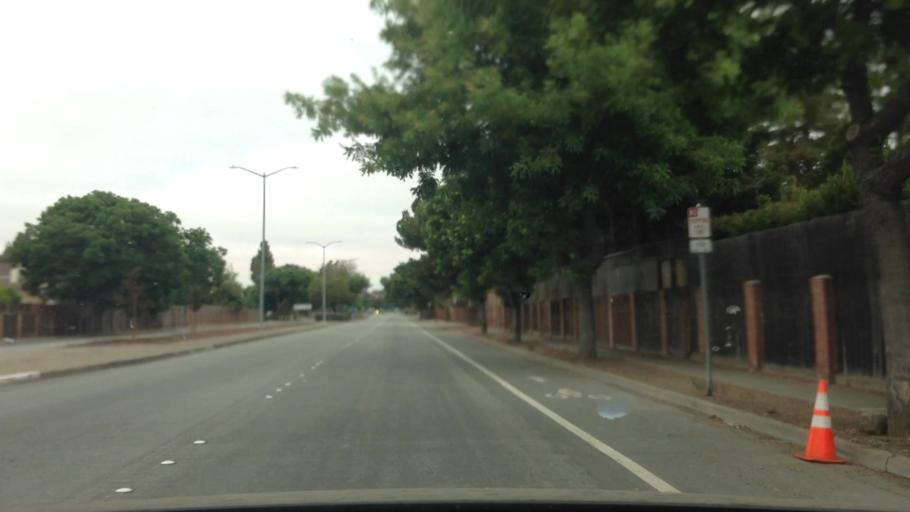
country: US
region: California
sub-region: Alameda County
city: Fremont
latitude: 37.5238
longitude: -121.9601
